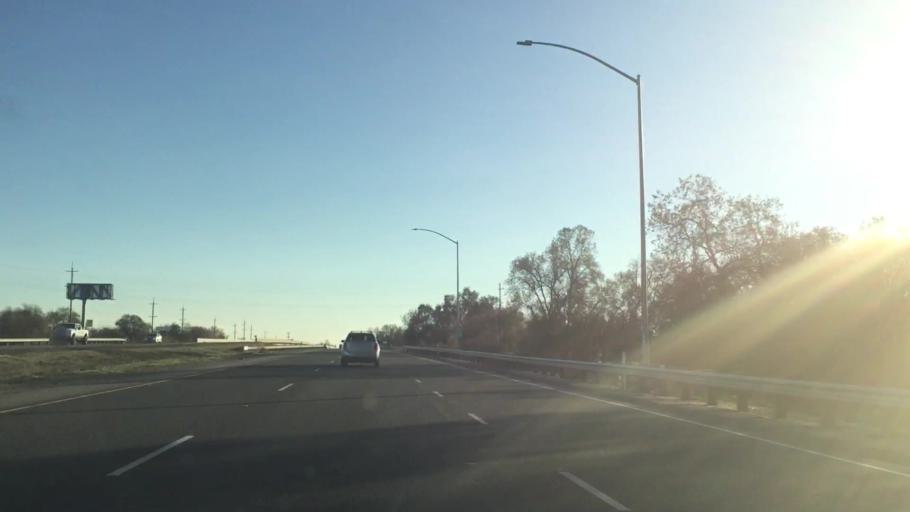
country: US
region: California
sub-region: Yuba County
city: Plumas Lake
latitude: 38.9754
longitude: -121.5433
